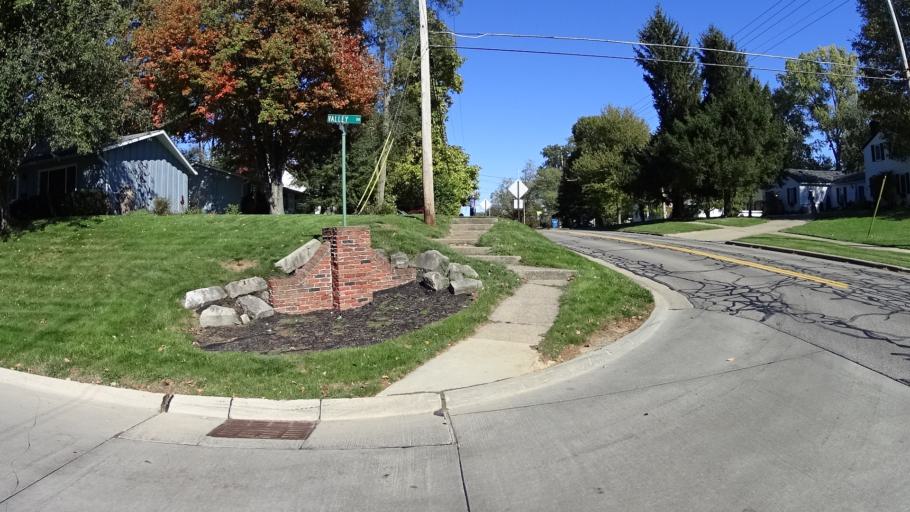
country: US
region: Ohio
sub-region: Lorain County
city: Amherst
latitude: 41.3912
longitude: -82.2396
